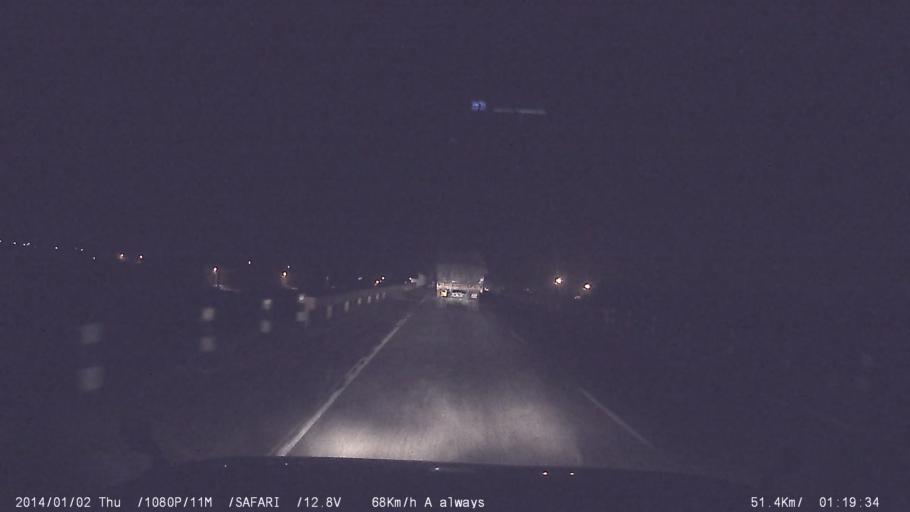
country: IN
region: Tamil Nadu
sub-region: Coimbatore
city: Irugur
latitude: 11.0219
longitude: 77.0752
